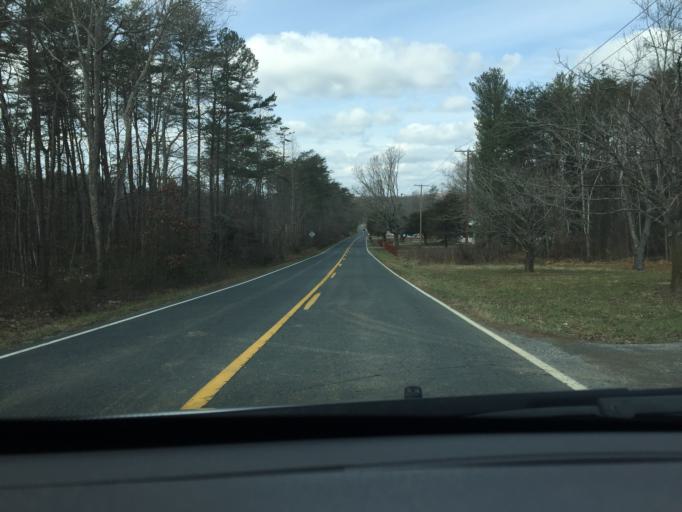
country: US
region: Virginia
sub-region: Campbell County
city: Rustburg
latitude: 37.3265
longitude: -79.1511
